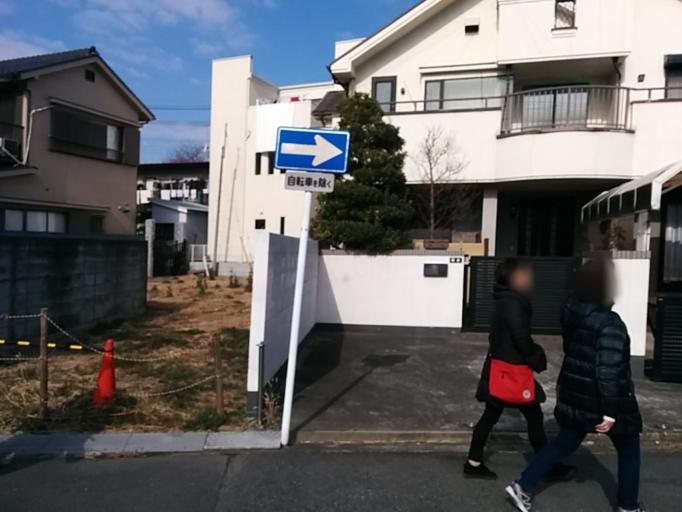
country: JP
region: Saitama
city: Kawagoe
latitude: 35.9197
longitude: 139.4896
